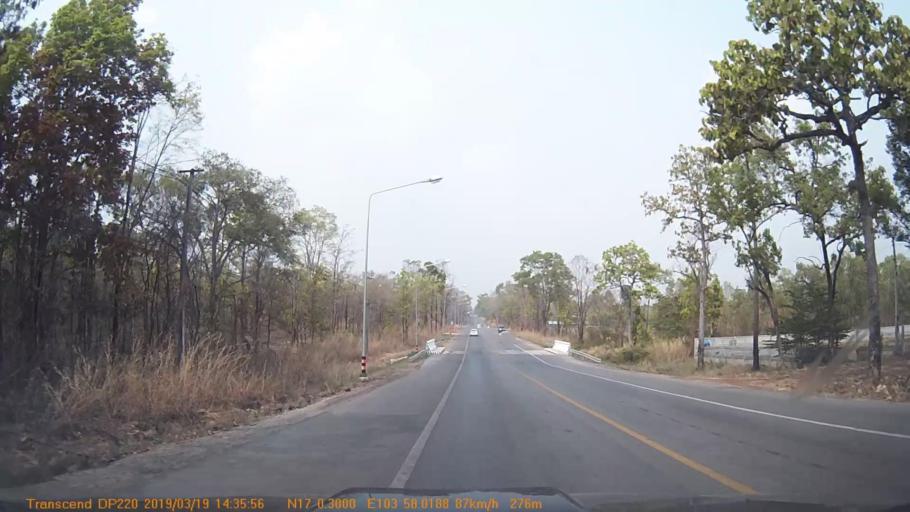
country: TH
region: Sakon Nakhon
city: Phu Phan
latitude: 17.0052
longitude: 103.9671
